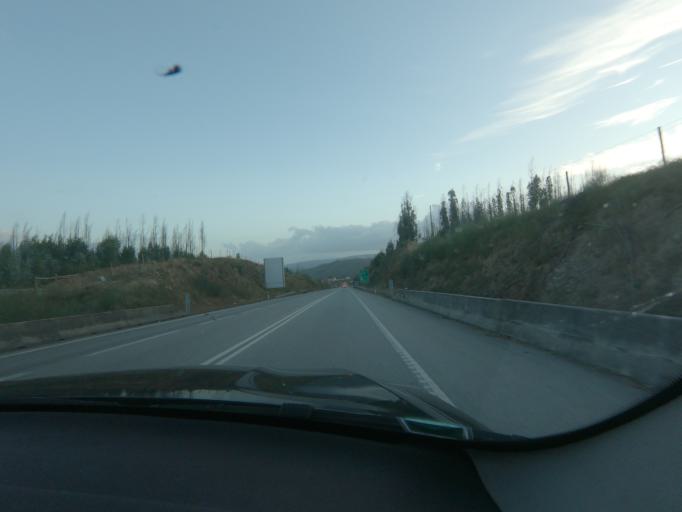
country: PT
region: Viseu
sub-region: Mortagua
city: Mortagua
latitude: 40.3453
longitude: -8.2110
